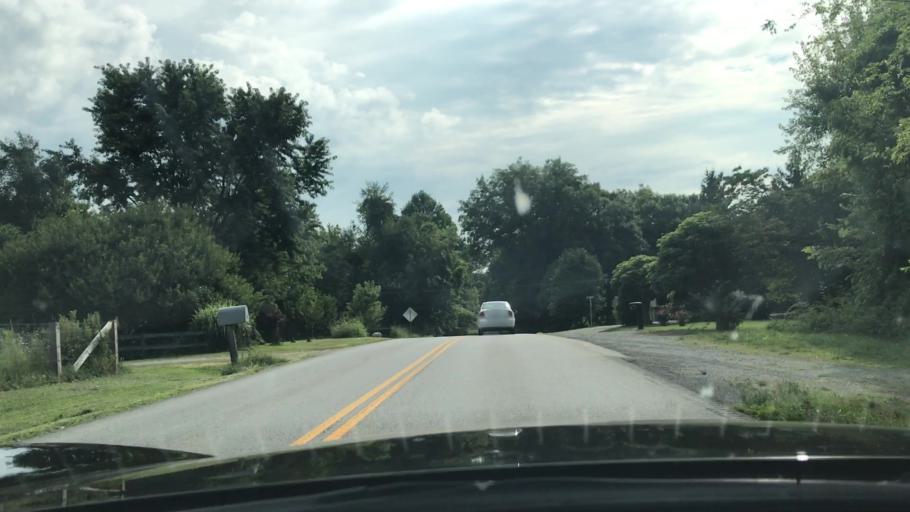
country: US
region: Kentucky
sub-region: Green County
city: Greensburg
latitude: 37.2678
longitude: -85.5411
